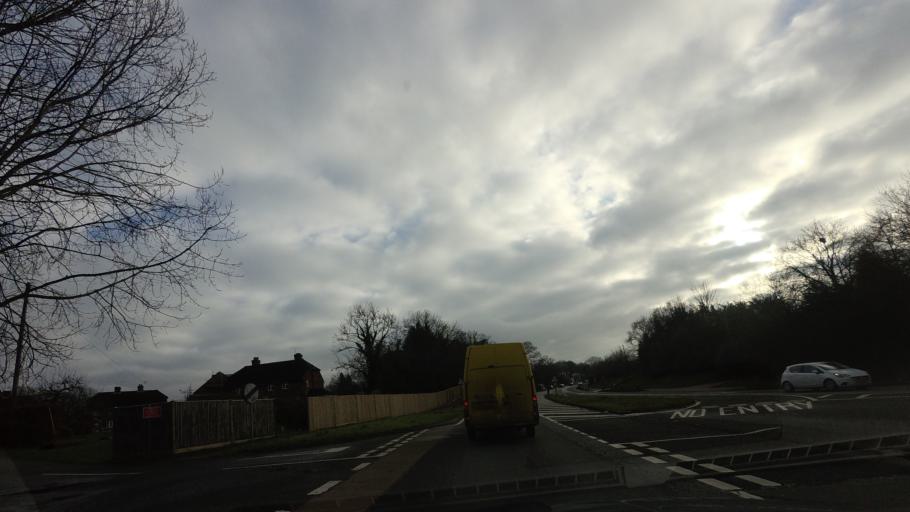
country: GB
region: England
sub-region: Kent
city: Hawkhurst
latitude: 51.0597
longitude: 0.4462
